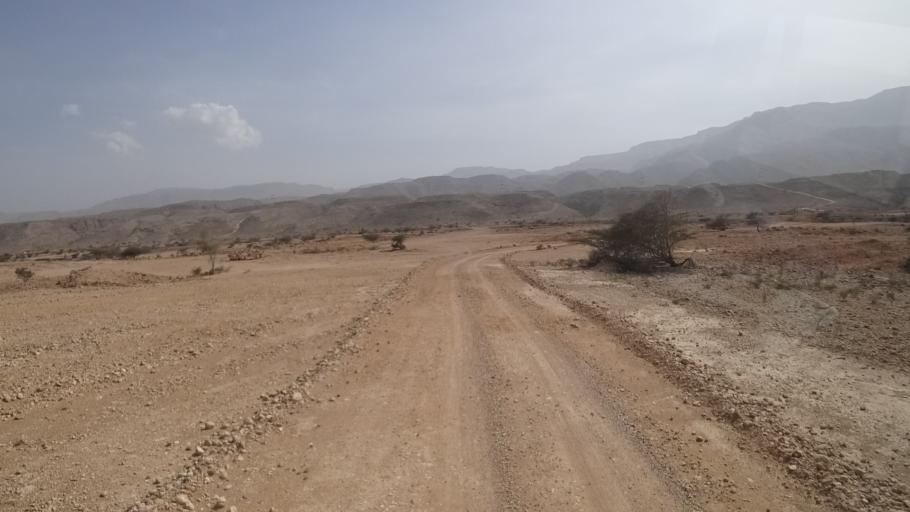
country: OM
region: Ash Sharqiyah
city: Sur
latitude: 22.9919
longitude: 59.1255
